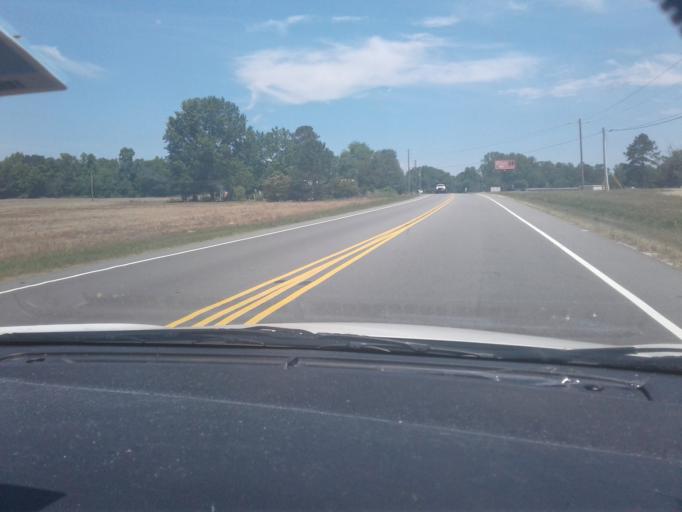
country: US
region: North Carolina
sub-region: Harnett County
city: Lillington
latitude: 35.4554
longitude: -78.8295
